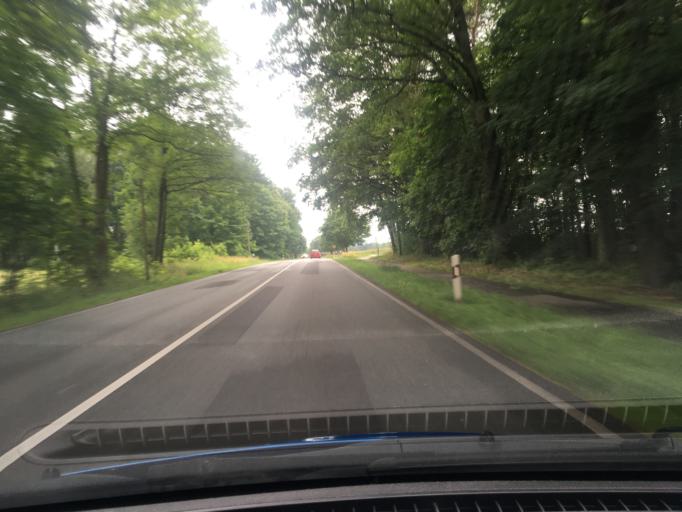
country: DE
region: Mecklenburg-Vorpommern
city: Stralendorf
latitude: 53.5593
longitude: 11.3413
